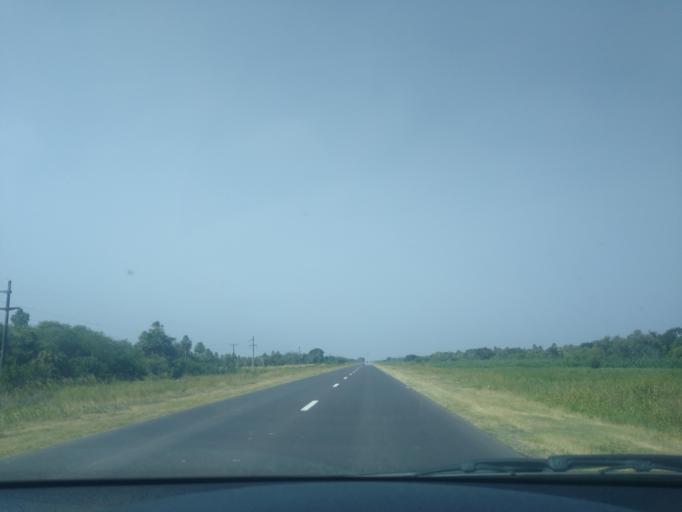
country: AR
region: Chaco
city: Fontana
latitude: -27.5536
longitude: -59.1437
